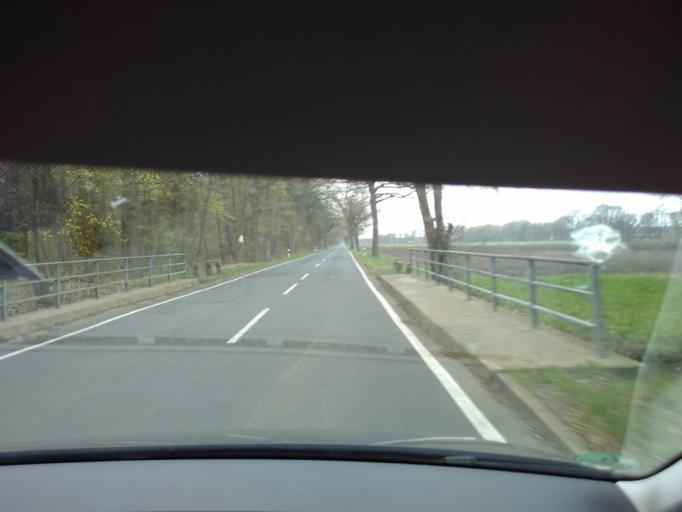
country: DE
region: Lower Saxony
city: Adelheidsdorf
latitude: 52.5913
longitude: 10.0451
